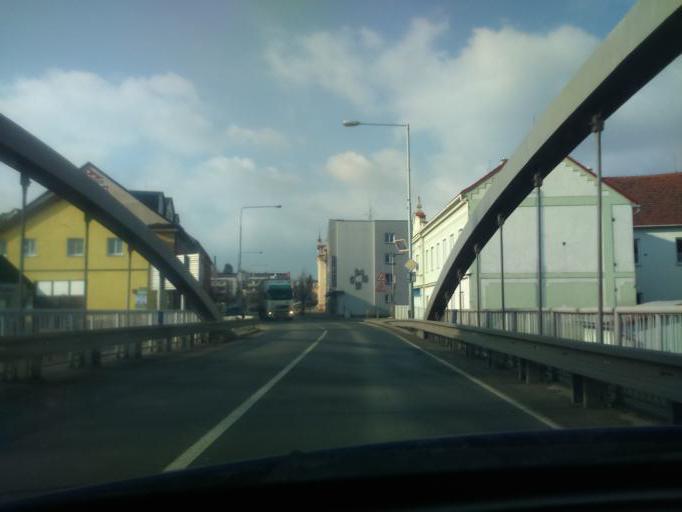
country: CZ
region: Plzensky
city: Stod
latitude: 49.6383
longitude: 13.1656
